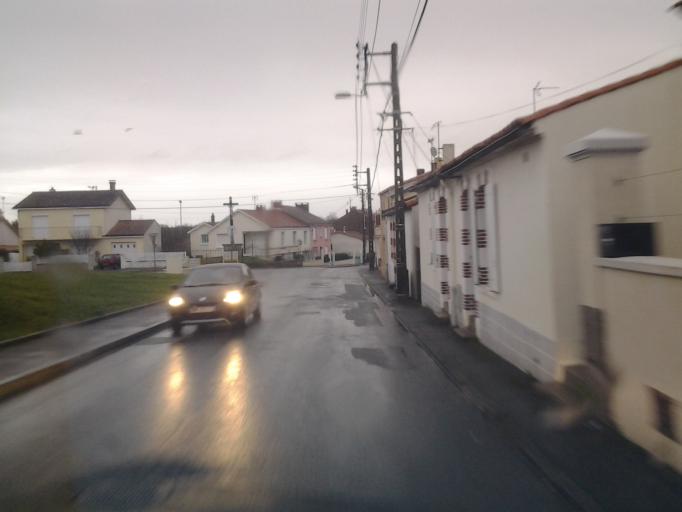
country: FR
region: Pays de la Loire
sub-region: Departement de la Vendee
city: La Roche-sur-Yon
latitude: 46.6664
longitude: -1.4515
